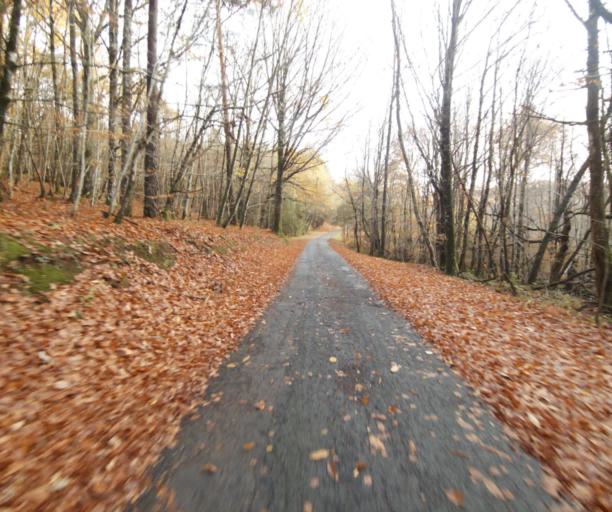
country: FR
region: Limousin
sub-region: Departement de la Correze
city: Cornil
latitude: 45.2008
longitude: 1.7013
